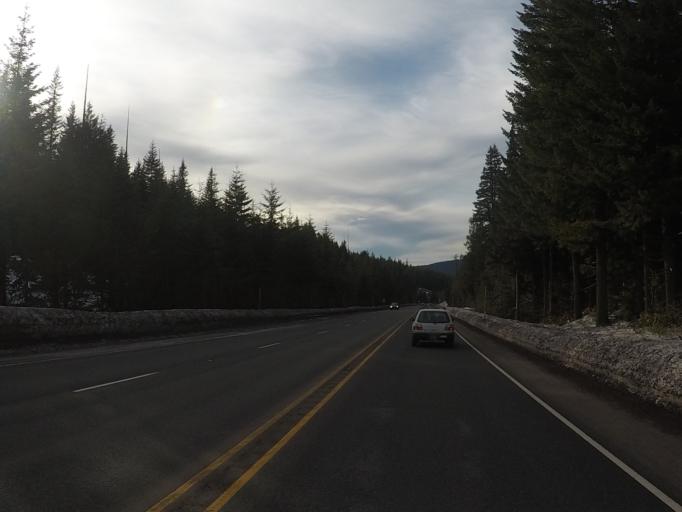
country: US
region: Oregon
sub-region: Clackamas County
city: Mount Hood Village
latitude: 45.3035
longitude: -121.7822
